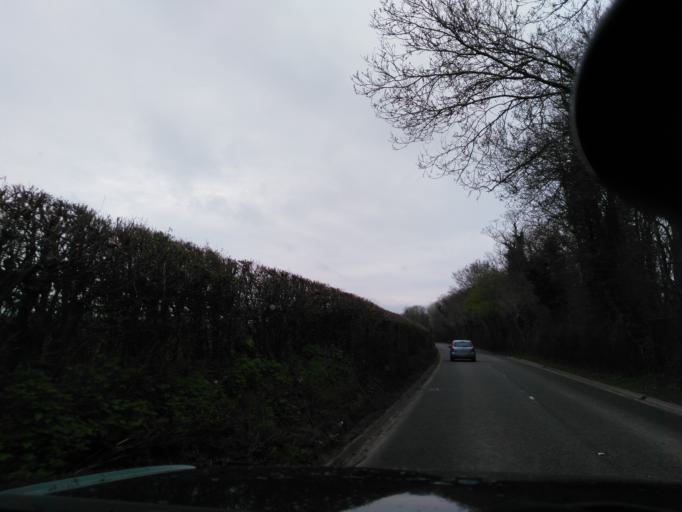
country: GB
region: England
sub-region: Wiltshire
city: Westwood
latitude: 51.3276
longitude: -2.2583
